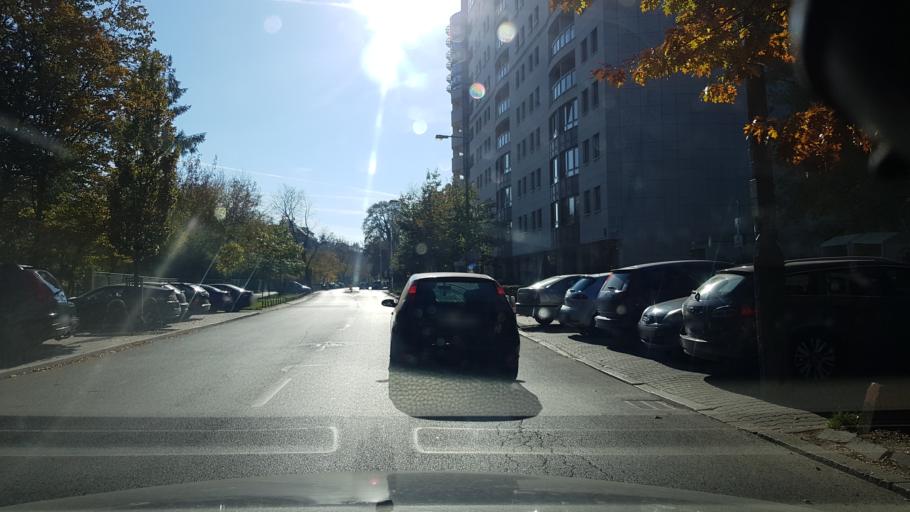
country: PL
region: Masovian Voivodeship
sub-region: Warszawa
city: Mokotow
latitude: 52.2034
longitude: 21.0153
